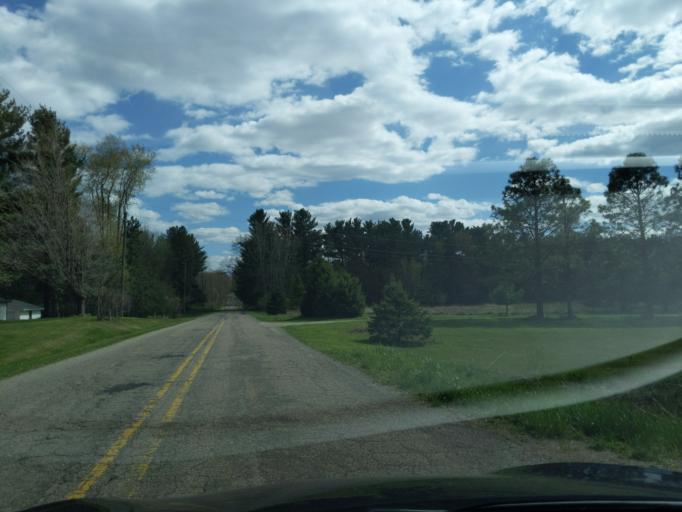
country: US
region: Michigan
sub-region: Ingham County
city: Leslie
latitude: 42.4078
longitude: -84.5269
